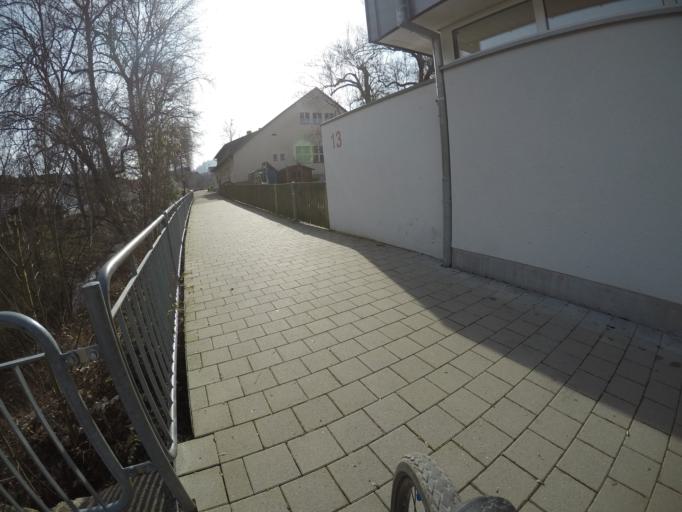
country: DE
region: Baden-Wuerttemberg
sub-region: Karlsruhe Region
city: Wildberg
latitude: 48.6172
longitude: 8.7792
